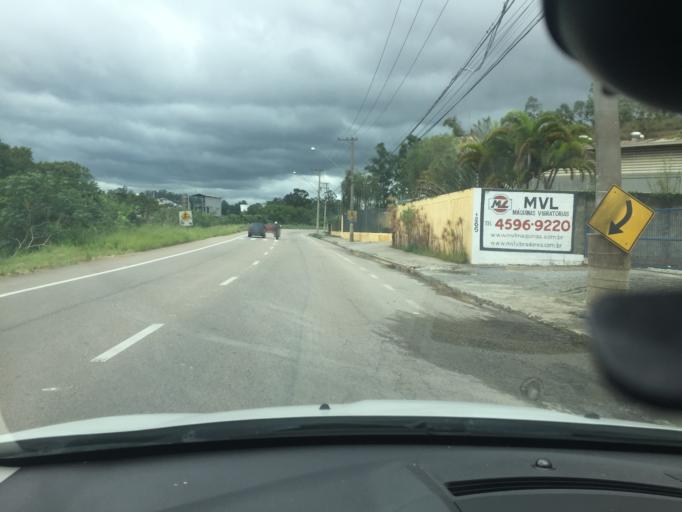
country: BR
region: Sao Paulo
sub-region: Varzea Paulista
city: Varzea Paulista
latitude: -23.2032
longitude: -46.8220
